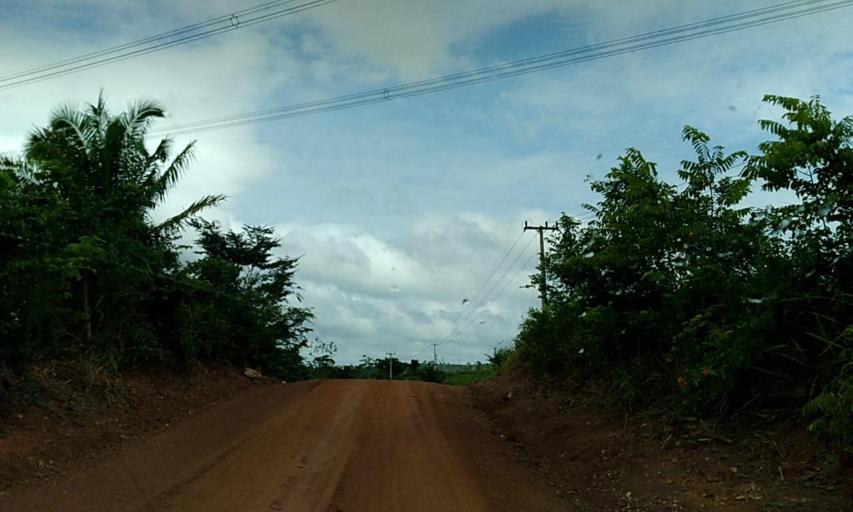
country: BR
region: Para
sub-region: Altamira
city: Altamira
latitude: -3.0911
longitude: -51.6334
